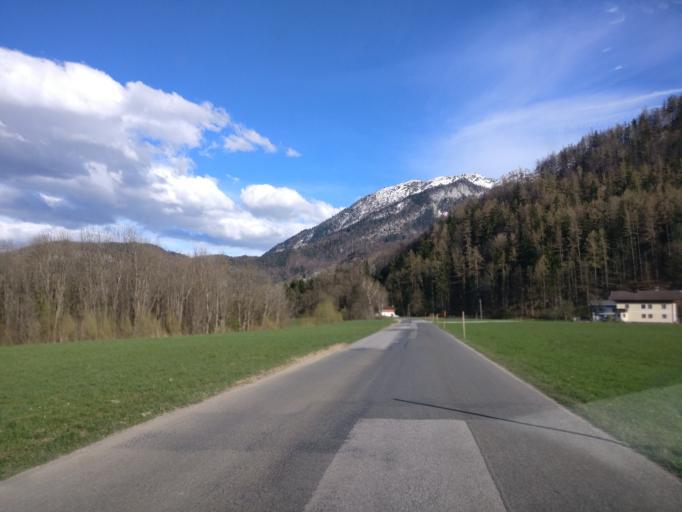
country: AT
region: Salzburg
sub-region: Politischer Bezirk Hallein
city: Golling an der Salzach
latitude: 47.5818
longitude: 13.1658
